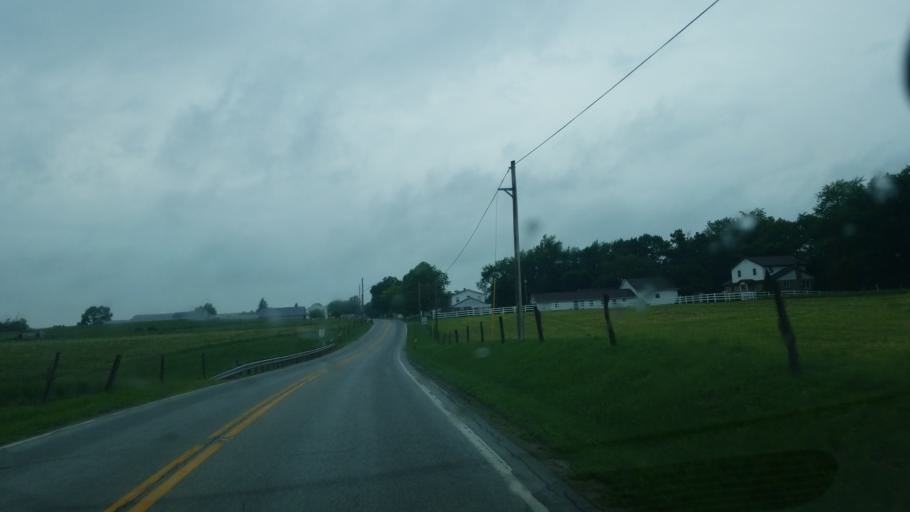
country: US
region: Ohio
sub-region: Tuscarawas County
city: Sugarcreek
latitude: 40.4811
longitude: -81.7238
